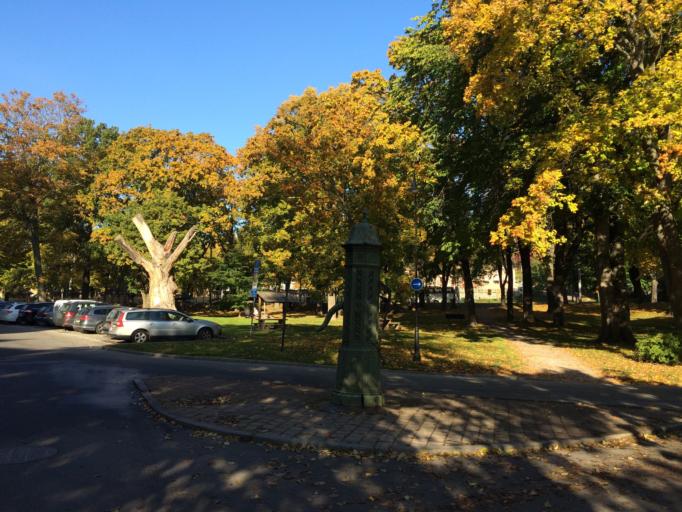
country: SE
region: Stockholm
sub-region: Stockholms Kommun
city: OEstermalm
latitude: 59.3229
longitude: 18.1015
